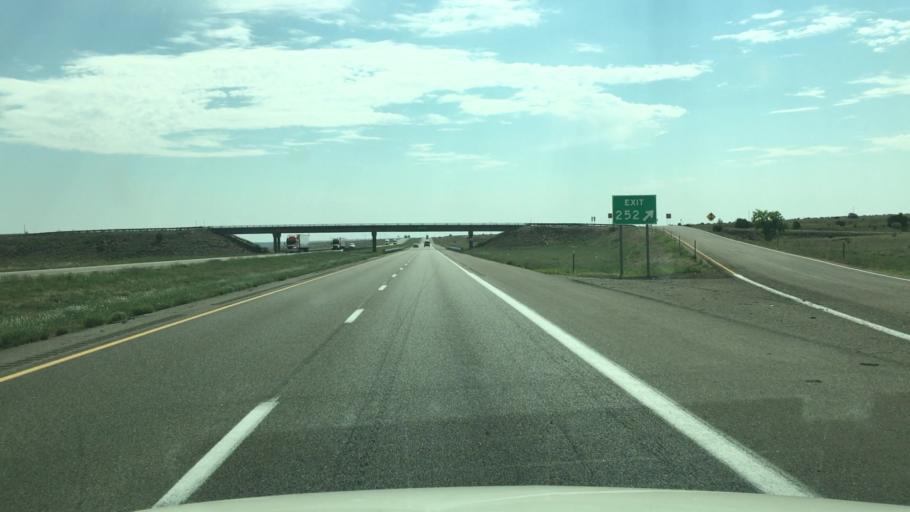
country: US
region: New Mexico
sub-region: Guadalupe County
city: Santa Rosa
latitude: 34.9802
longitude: -105.0690
